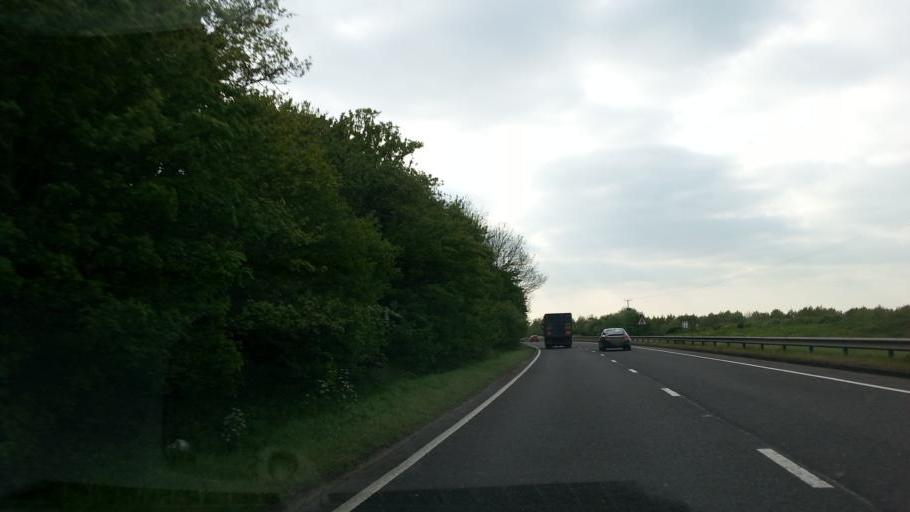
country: GB
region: England
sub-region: Nottinghamshire
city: South Collingham
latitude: 53.0753
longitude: -0.6917
